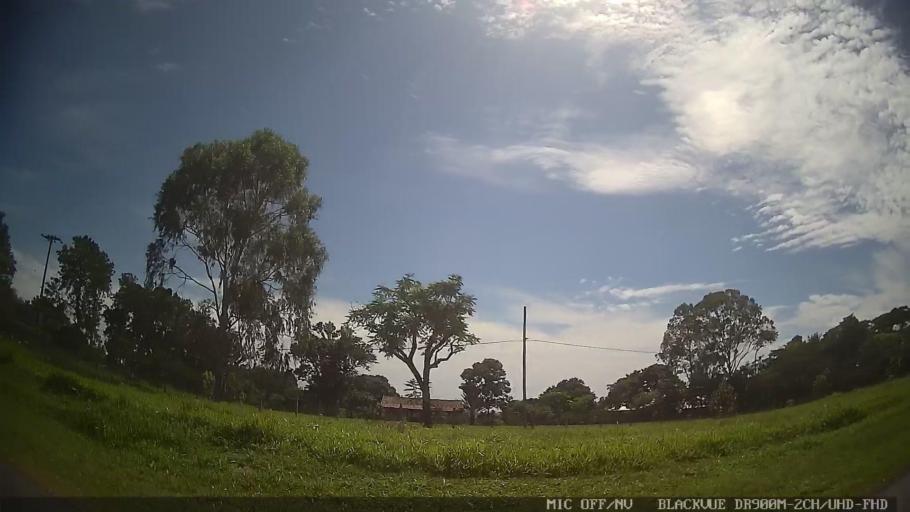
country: BR
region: Sao Paulo
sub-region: Cerquilho
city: Cerquilho
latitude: -23.1789
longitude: -47.6398
